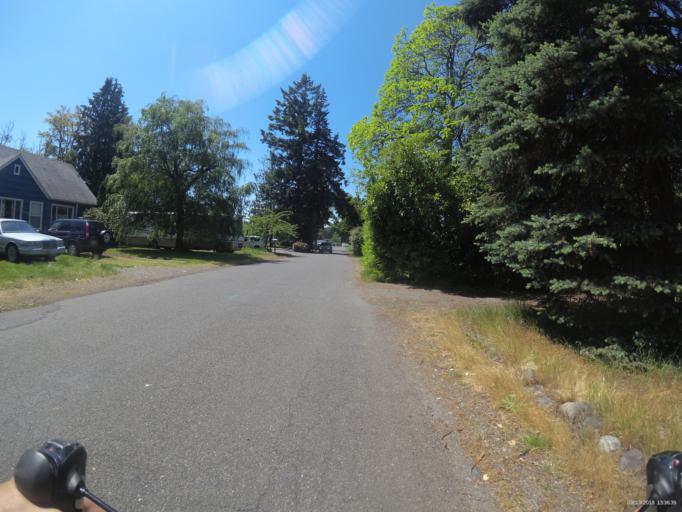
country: US
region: Washington
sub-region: Pierce County
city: Lakewood
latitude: 47.1677
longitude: -122.5174
